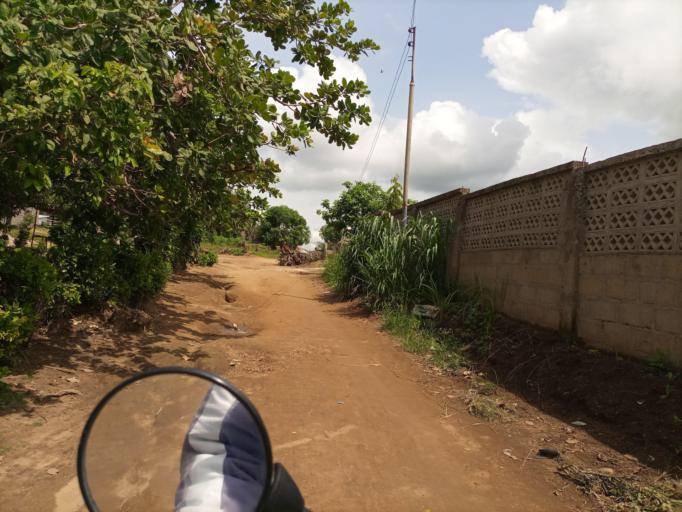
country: SL
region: Southern Province
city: Bo
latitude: 7.9717
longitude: -11.7665
